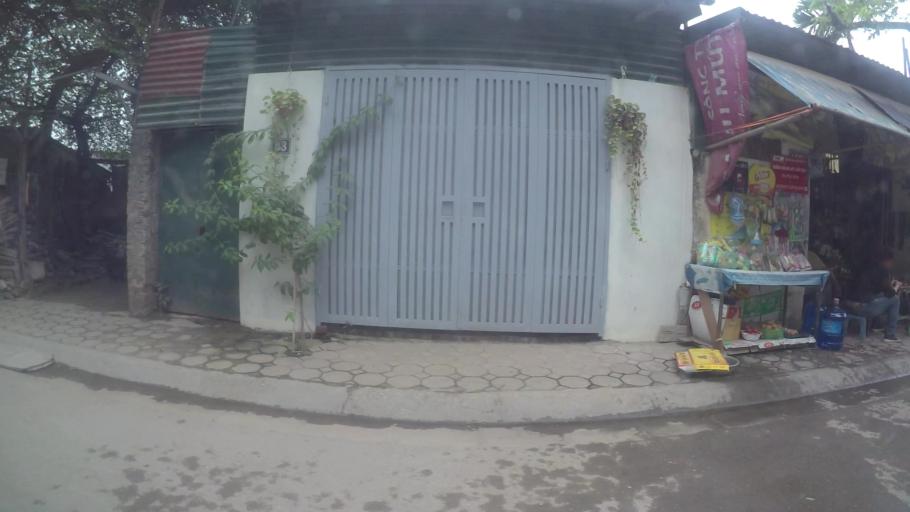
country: VN
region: Ha Noi
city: Tay Ho
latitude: 21.0777
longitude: 105.8239
